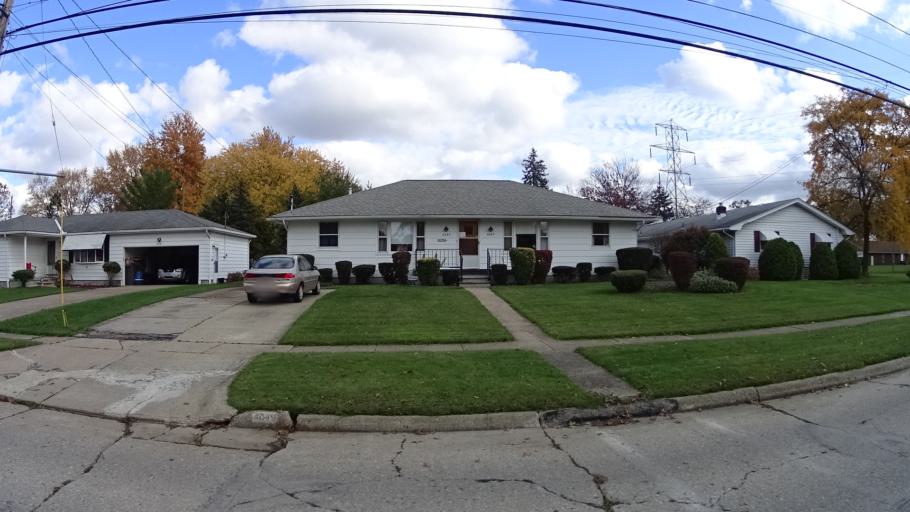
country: US
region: Ohio
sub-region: Lorain County
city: Lorain
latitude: 41.4335
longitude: -82.1898
